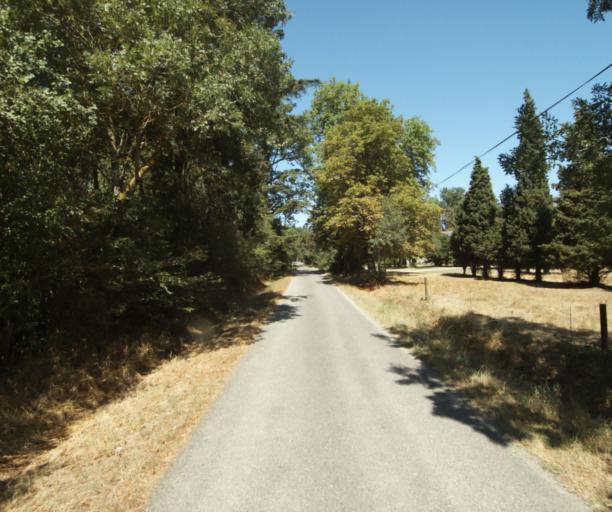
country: FR
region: Midi-Pyrenees
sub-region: Departement de la Haute-Garonne
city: Revel
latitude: 43.4813
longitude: 1.9716
